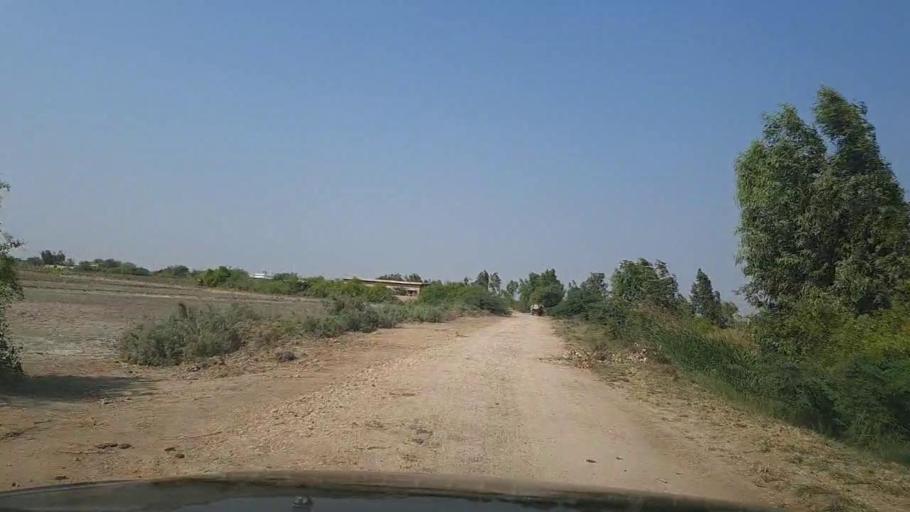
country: PK
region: Sindh
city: Thatta
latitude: 24.6435
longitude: 67.8069
